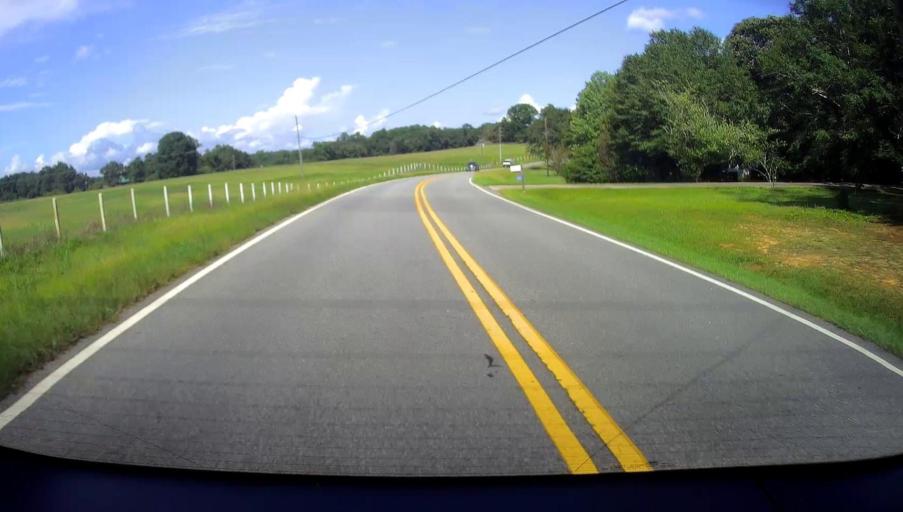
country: US
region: Georgia
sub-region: Upson County
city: Hannahs Mill
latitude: 32.9508
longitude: -84.3210
